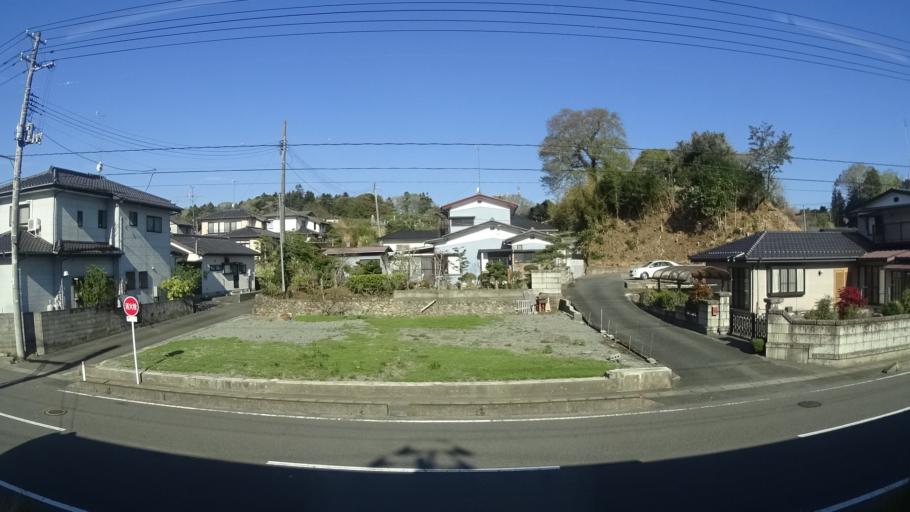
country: JP
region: Fukushima
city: Namie
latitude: 37.5559
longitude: 140.9953
